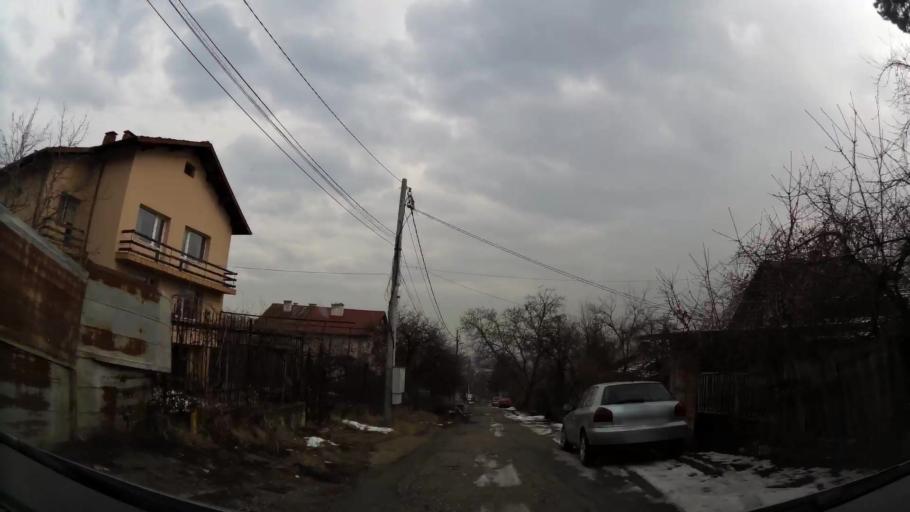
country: BG
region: Sofia-Capital
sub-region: Stolichna Obshtina
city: Sofia
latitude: 42.6665
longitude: 23.2443
